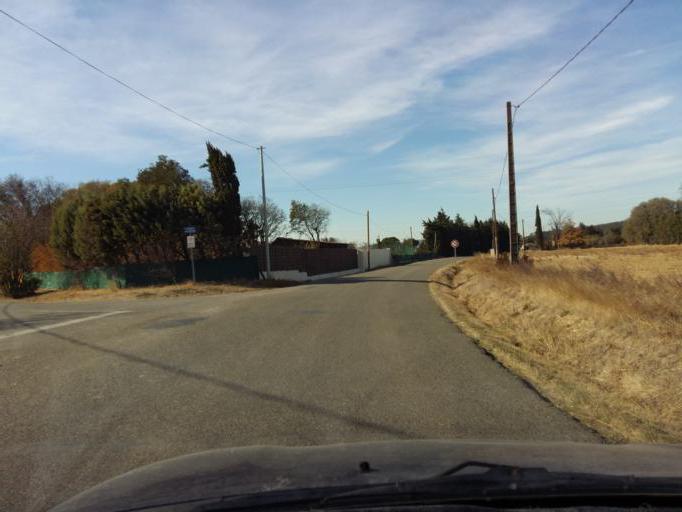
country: FR
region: Provence-Alpes-Cote d'Azur
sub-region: Departement du Vaucluse
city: Piolenc
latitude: 44.1806
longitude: 4.7865
